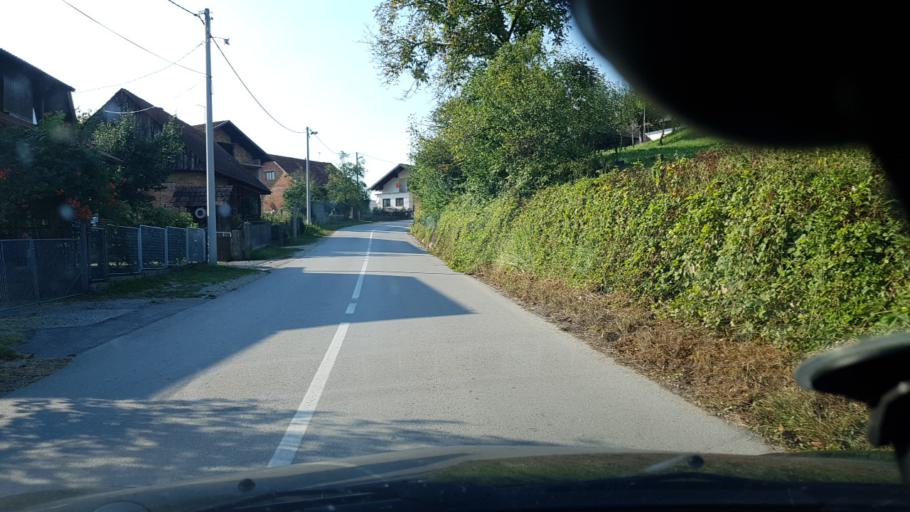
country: HR
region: Zagrebacka
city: Pojatno
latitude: 45.9418
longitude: 15.7295
